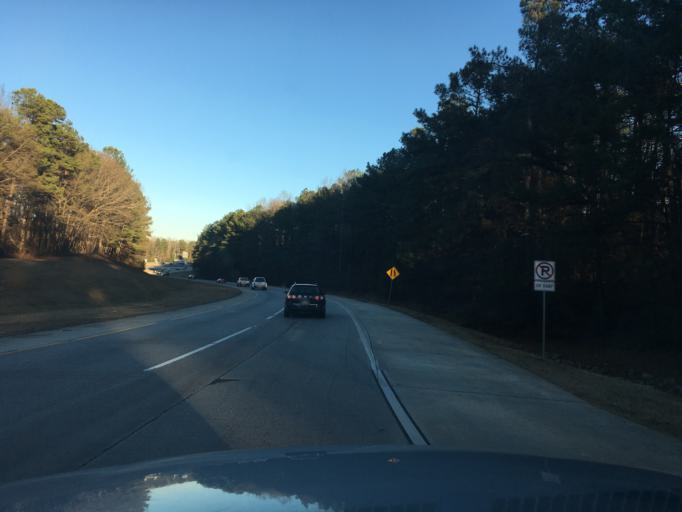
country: US
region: Georgia
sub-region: Carroll County
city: Villa Rica
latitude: 33.7208
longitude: -84.9387
